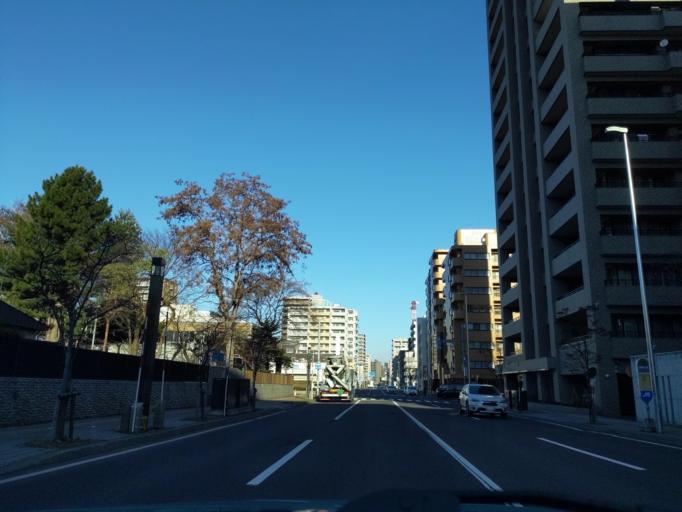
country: JP
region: Hokkaido
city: Sapporo
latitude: 43.0614
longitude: 141.3341
